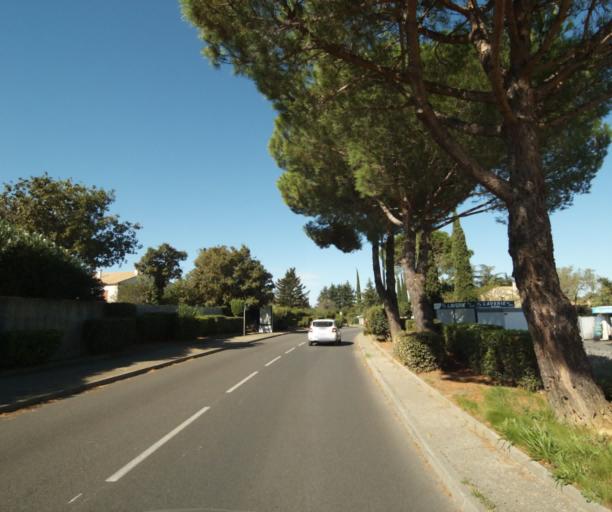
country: FR
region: Languedoc-Roussillon
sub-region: Departement du Gard
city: Bouillargues
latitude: 43.8003
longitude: 4.4178
